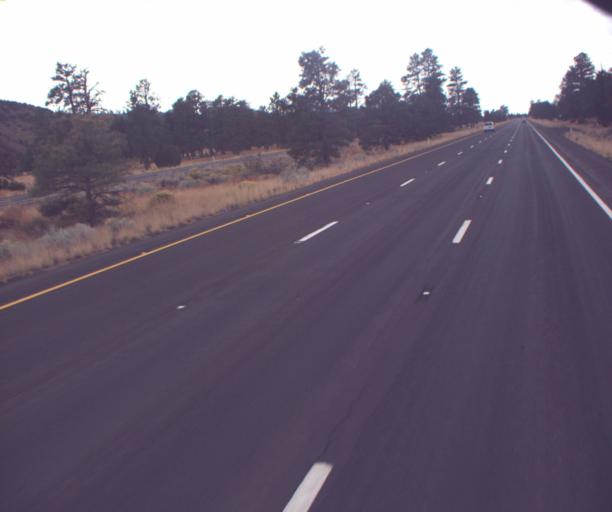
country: US
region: Arizona
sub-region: Coconino County
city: Flagstaff
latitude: 35.3967
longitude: -111.5773
